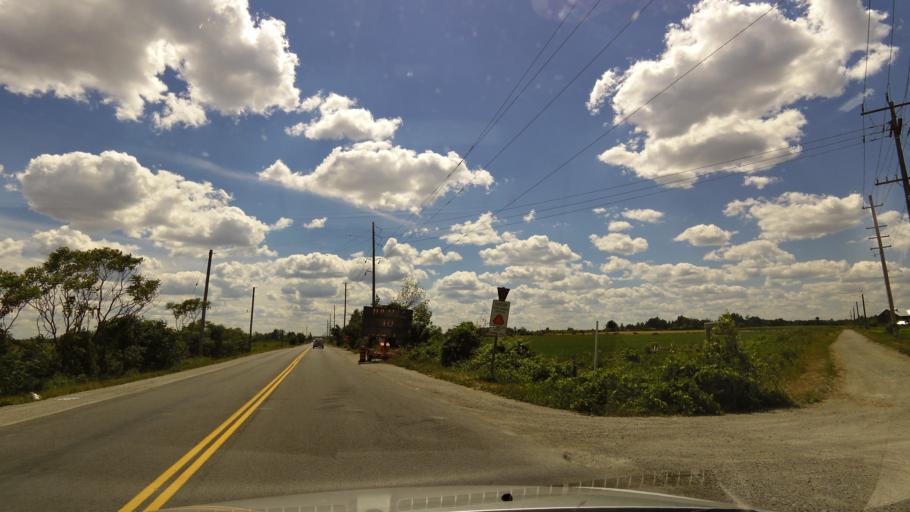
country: CA
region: Ontario
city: Brampton
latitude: 43.6426
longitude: -79.8575
